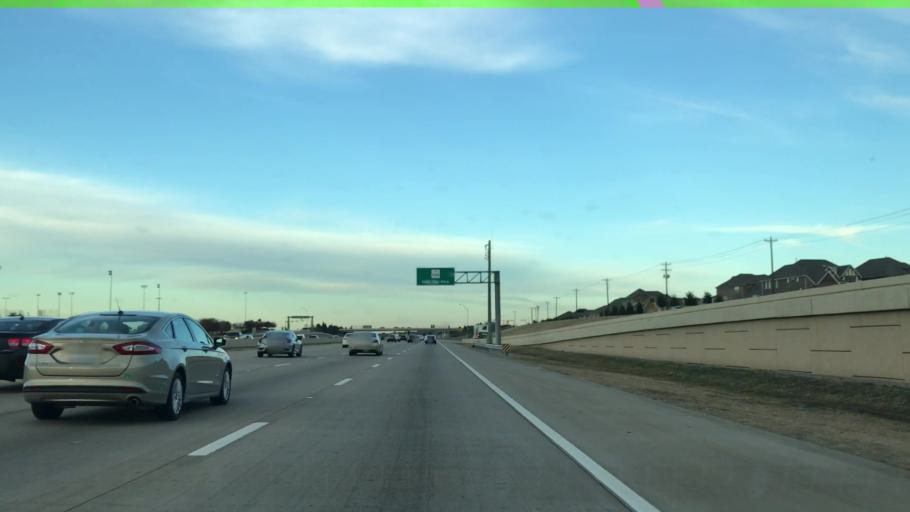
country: US
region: Texas
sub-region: Denton County
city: Lewisville
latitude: 33.0308
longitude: -96.9280
